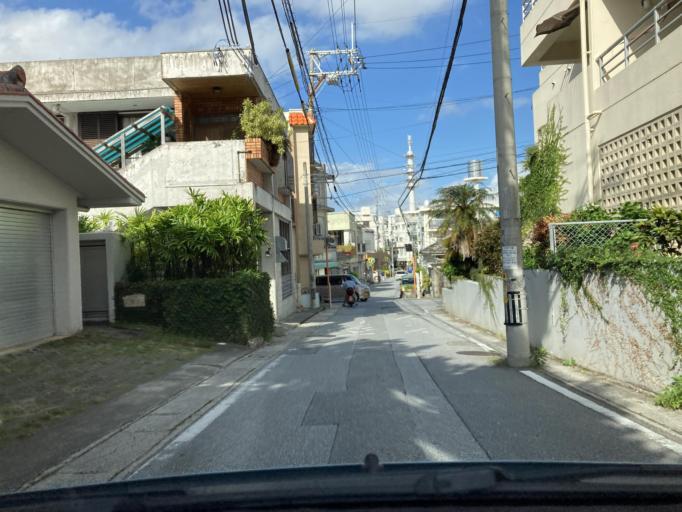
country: JP
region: Okinawa
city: Naha-shi
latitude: 26.2170
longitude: 127.7230
